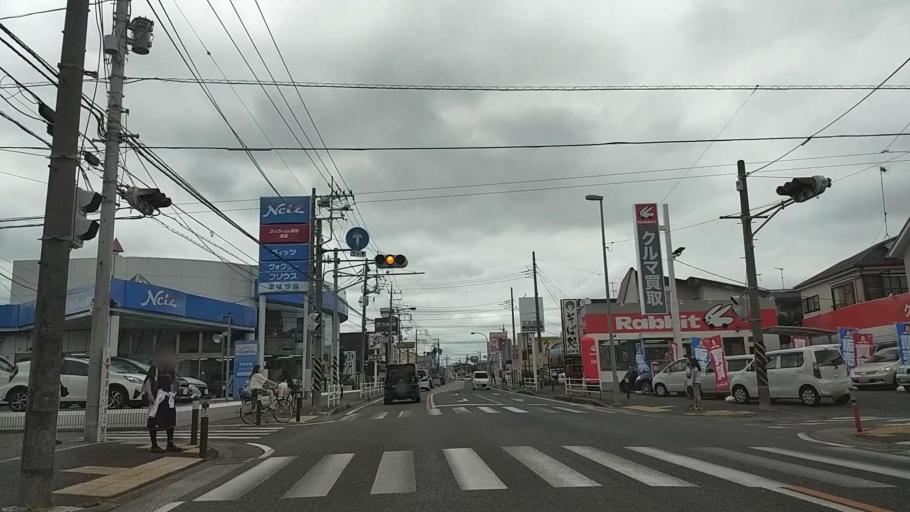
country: JP
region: Kanagawa
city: Minami-rinkan
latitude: 35.4194
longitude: 139.4691
